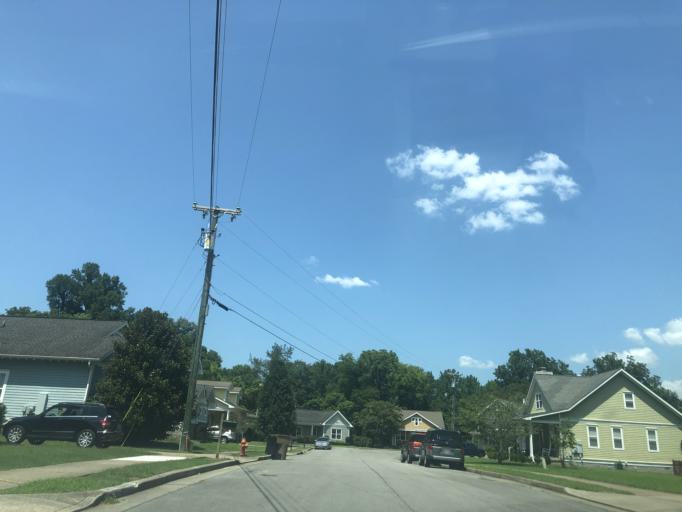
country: US
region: Tennessee
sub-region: Davidson County
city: Nashville
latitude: 36.1813
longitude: -86.7103
